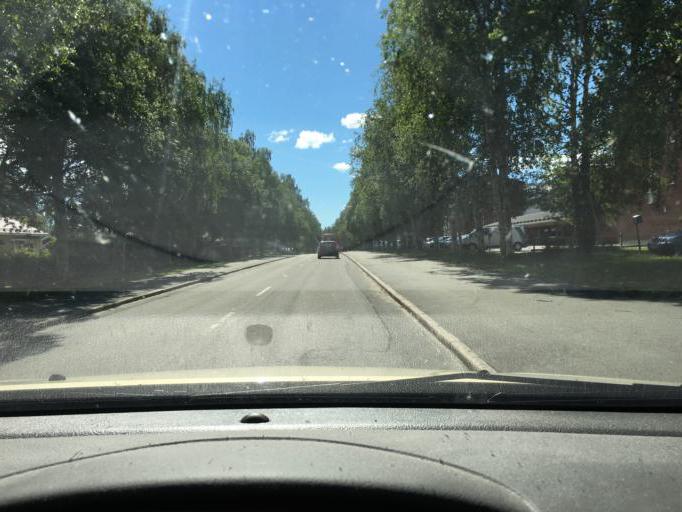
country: SE
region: Norrbotten
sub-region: Lulea Kommun
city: Lulea
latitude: 65.5997
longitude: 22.1333
